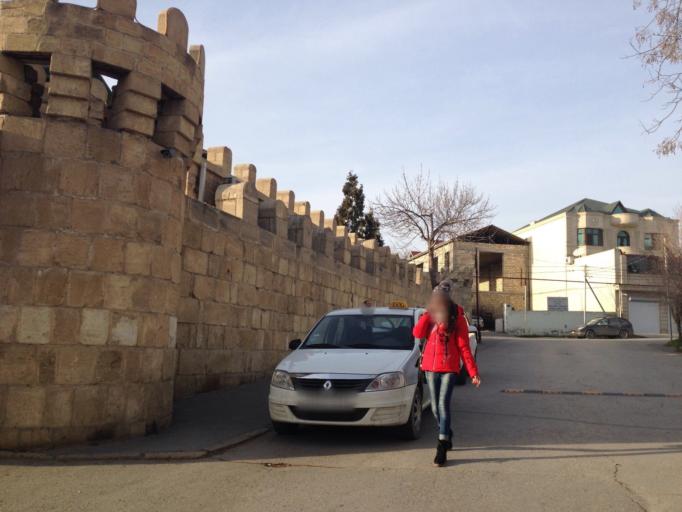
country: AZ
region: Baki
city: Baku
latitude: 40.3939
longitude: 49.8567
